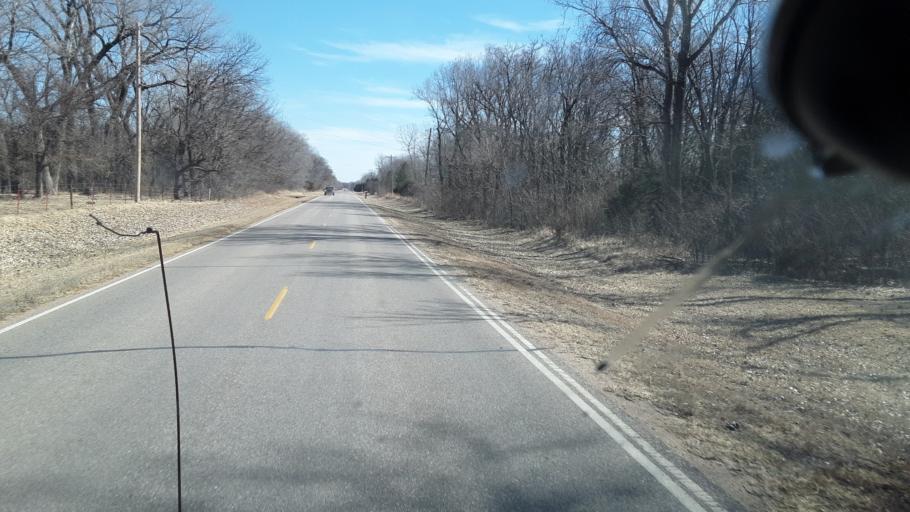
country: US
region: Kansas
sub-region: Reno County
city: Buhler
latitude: 38.1593
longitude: -97.8764
